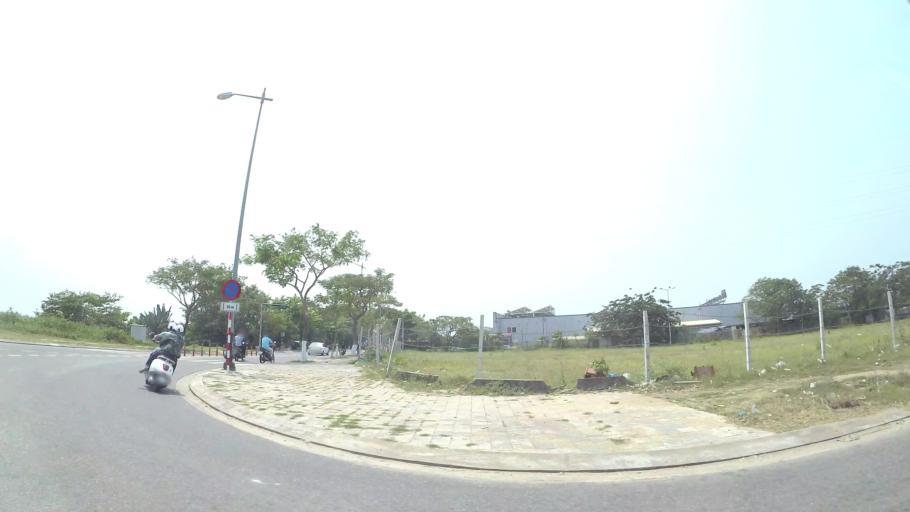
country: VN
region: Da Nang
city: Cam Le
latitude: 16.0253
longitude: 108.2218
